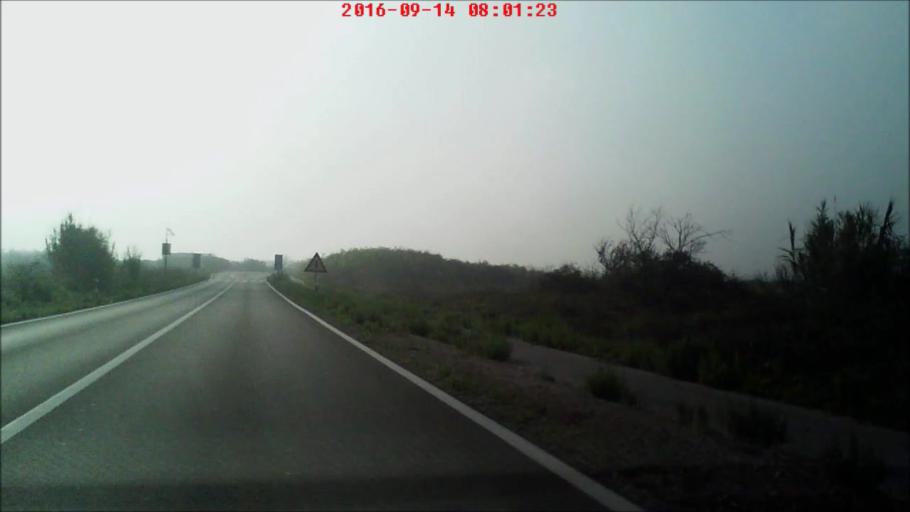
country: HR
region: Zadarska
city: Nin
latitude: 44.2523
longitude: 15.1600
